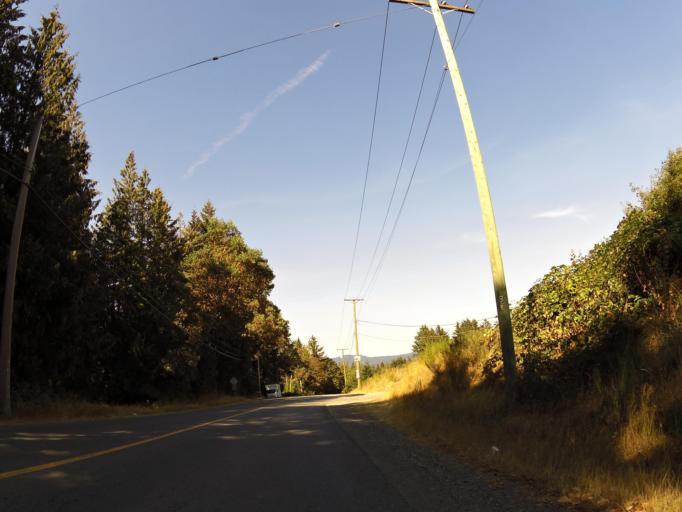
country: CA
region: British Columbia
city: North Saanich
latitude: 48.6736
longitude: -123.5524
